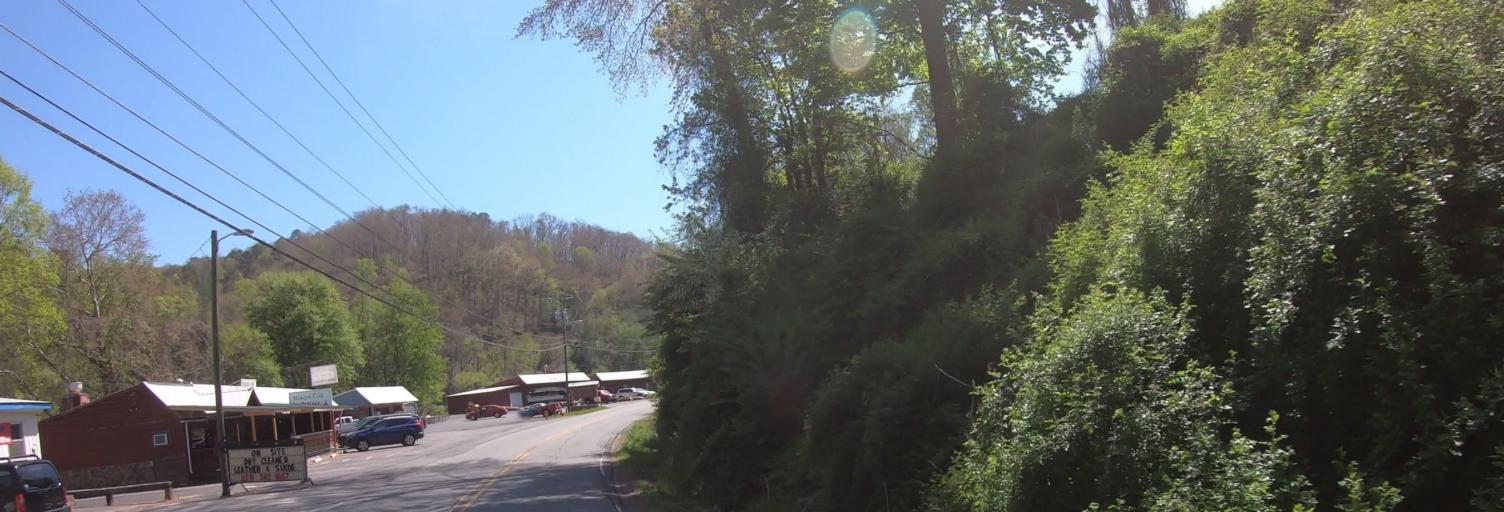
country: US
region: North Carolina
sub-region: Swain County
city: Bryson City
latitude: 35.4328
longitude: -83.4283
